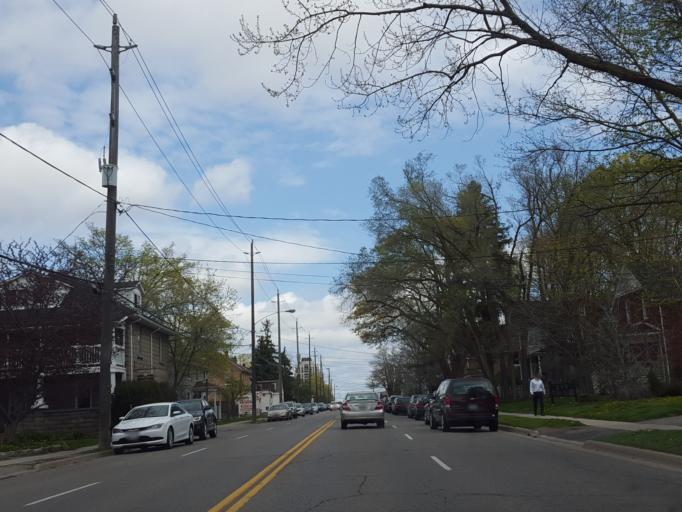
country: CA
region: Ontario
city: Markham
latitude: 43.8870
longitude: -79.2629
